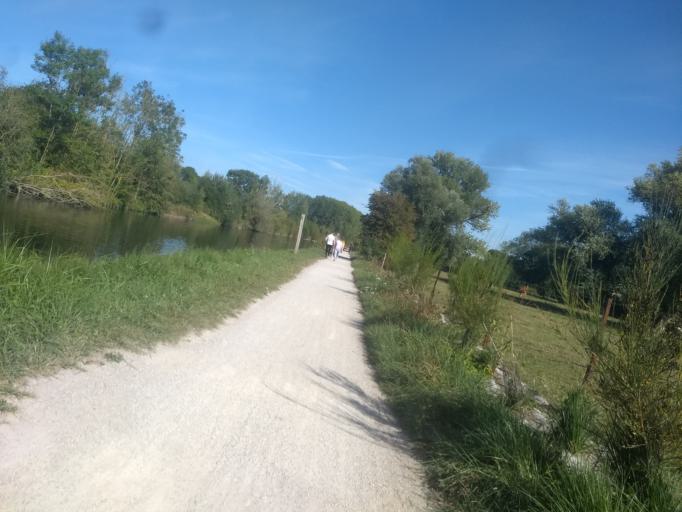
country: FR
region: Nord-Pas-de-Calais
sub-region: Departement du Pas-de-Calais
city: Feuchy
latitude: 50.2961
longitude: 2.8496
